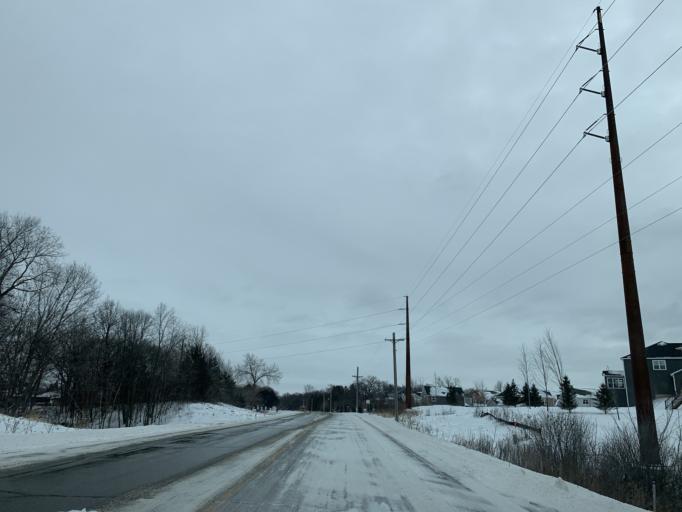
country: US
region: Minnesota
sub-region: Carver County
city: Chaska
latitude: 44.7893
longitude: -93.6206
